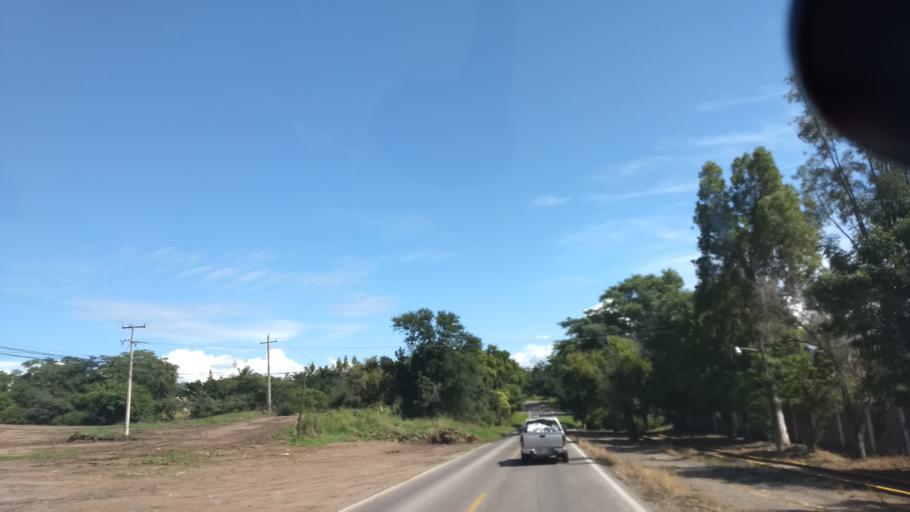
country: MX
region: Jalisco
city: Tuxpan
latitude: 19.5501
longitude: -103.3929
